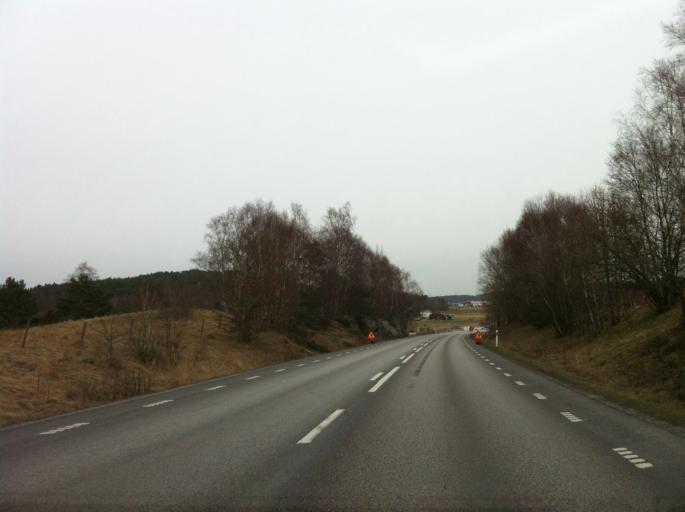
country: SE
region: Vaestra Goetaland
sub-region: Tjorns Kommun
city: Myggenas
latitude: 58.0066
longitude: 11.6710
